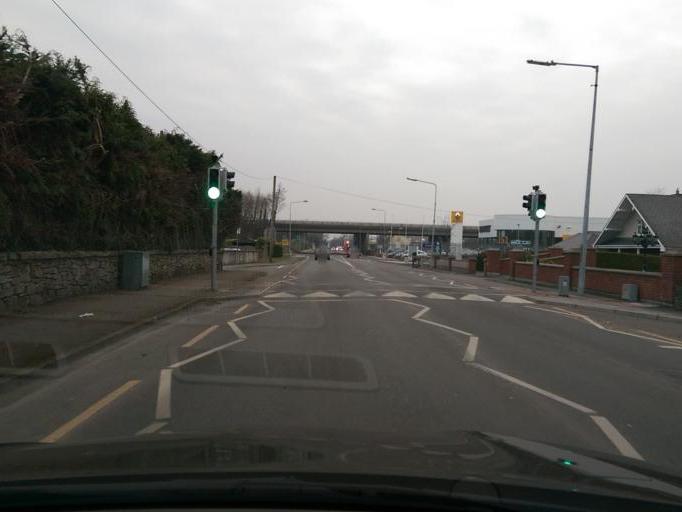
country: IE
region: Leinster
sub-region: An Iarmhi
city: Athlone
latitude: 53.4274
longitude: -7.9605
